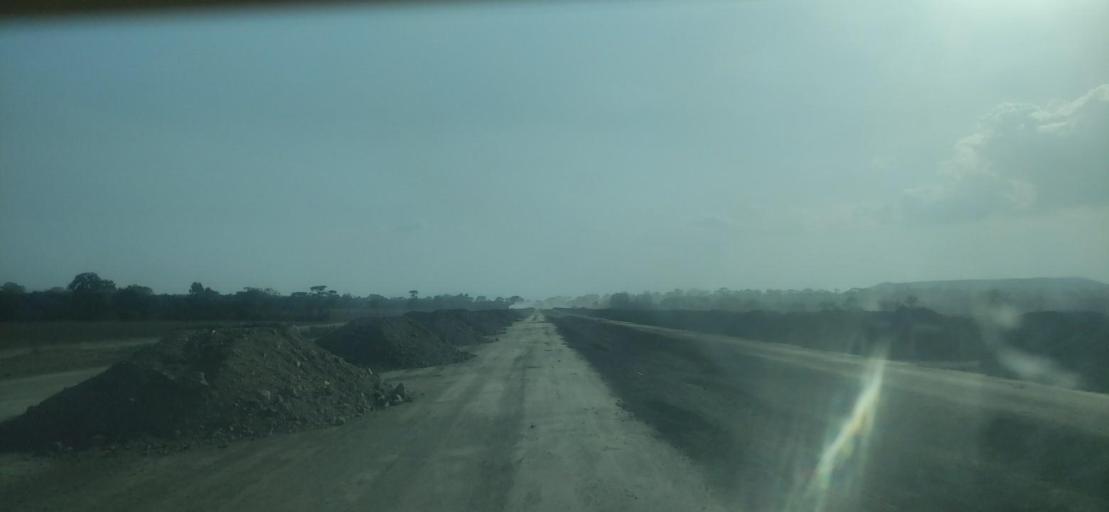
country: ET
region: Southern Nations, Nationalities, and People's Region
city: Hawassa
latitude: 7.1651
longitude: 38.4857
